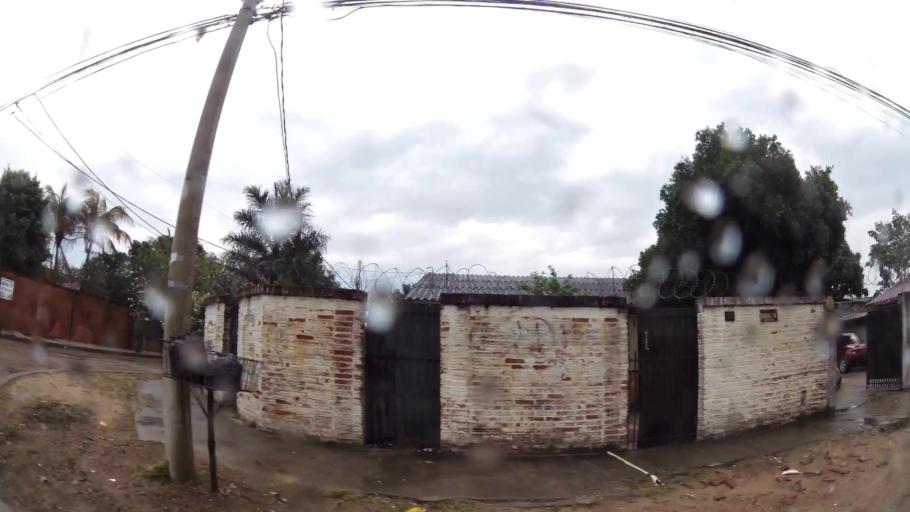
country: BO
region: Santa Cruz
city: Santa Cruz de la Sierra
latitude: -17.8046
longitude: -63.1557
